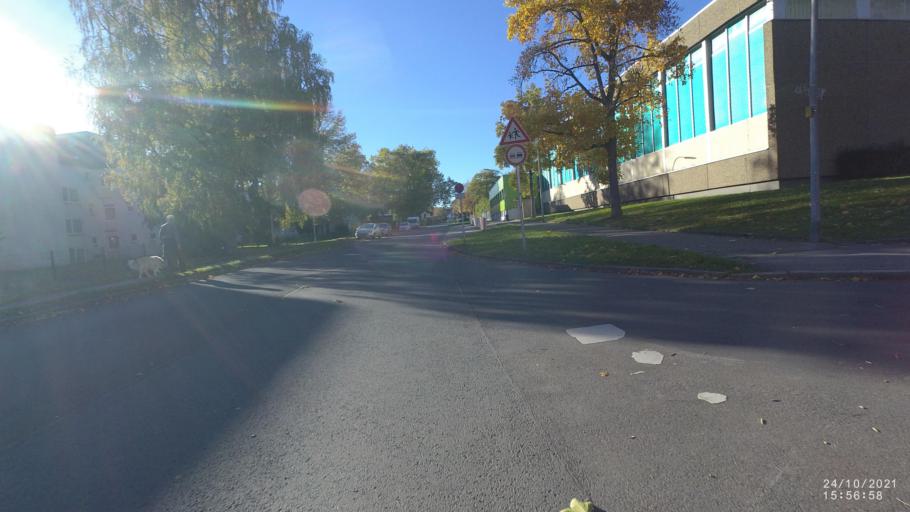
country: DE
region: North Rhine-Westphalia
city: Hemer
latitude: 51.3871
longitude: 7.7570
